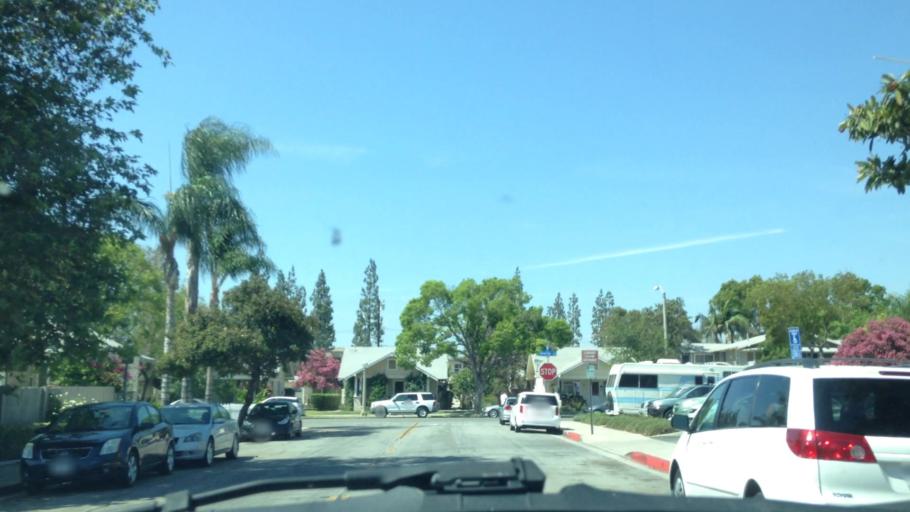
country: US
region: California
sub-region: Orange County
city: Fullerton
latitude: 33.8707
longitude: -117.9314
